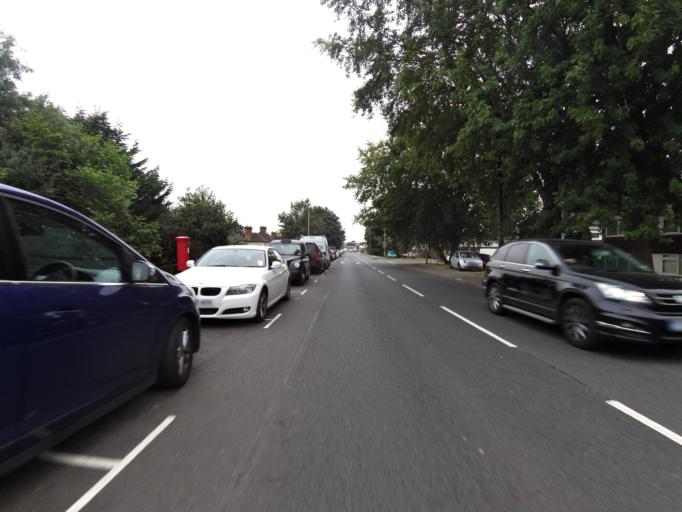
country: GB
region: England
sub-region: Hertfordshire
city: St Albans
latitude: 51.7284
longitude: -0.3003
